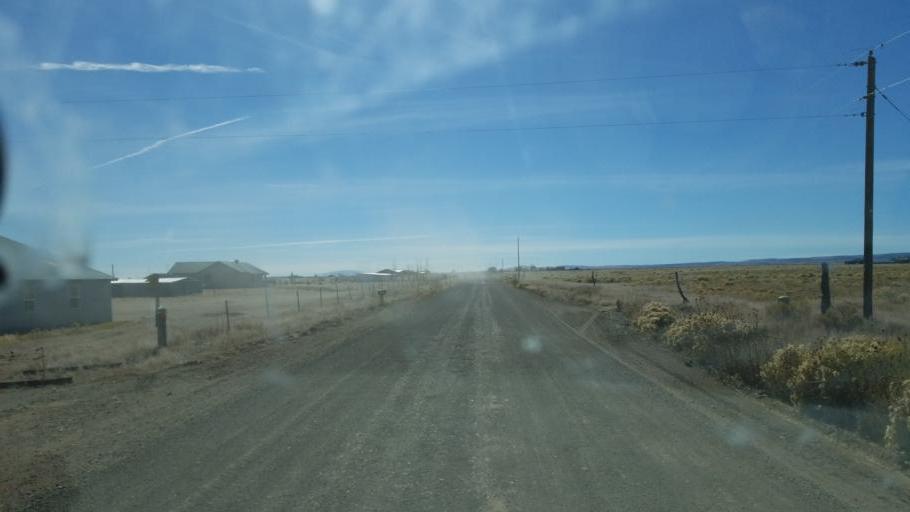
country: US
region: Colorado
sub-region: Rio Grande County
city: Monte Vista
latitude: 37.3874
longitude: -106.1494
